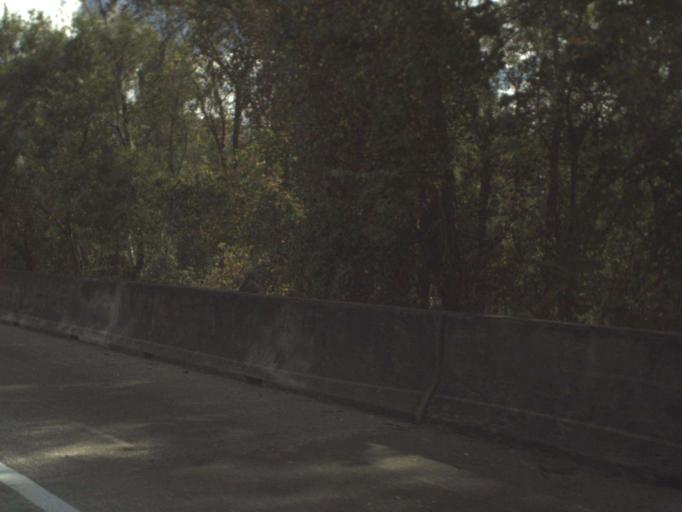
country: US
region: Florida
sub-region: Jackson County
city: Sneads
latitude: 30.6343
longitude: -84.9066
